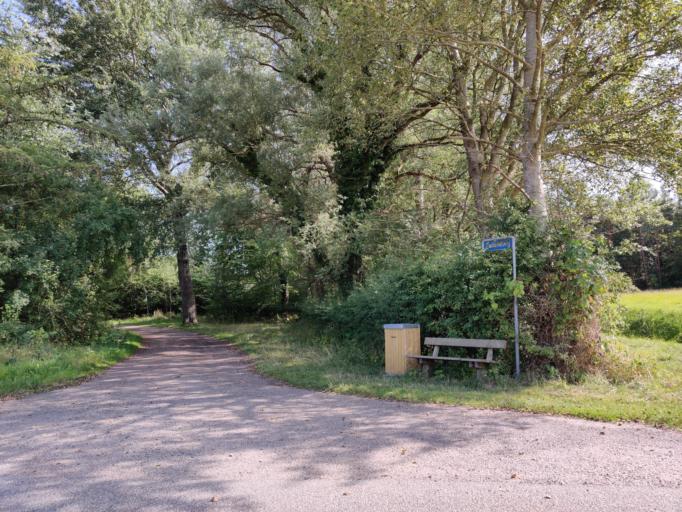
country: DK
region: Zealand
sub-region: Guldborgsund Kommune
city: Nykobing Falster
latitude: 54.6030
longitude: 11.9468
